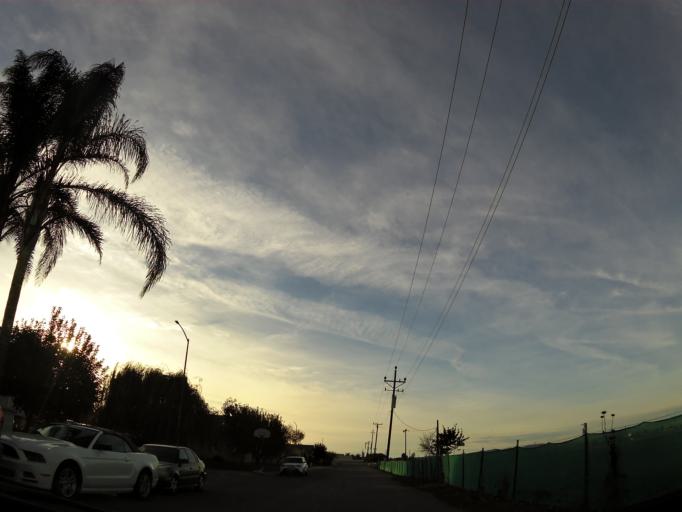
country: US
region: California
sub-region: San Benito County
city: Hollister
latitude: 36.8628
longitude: -121.3962
